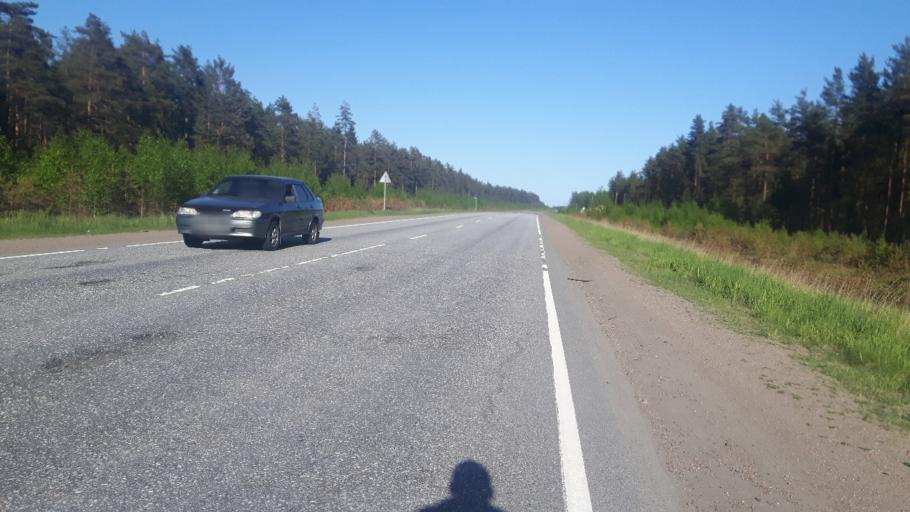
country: RU
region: Leningrad
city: Sosnovyy Bor
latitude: 60.1696
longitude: 29.1960
